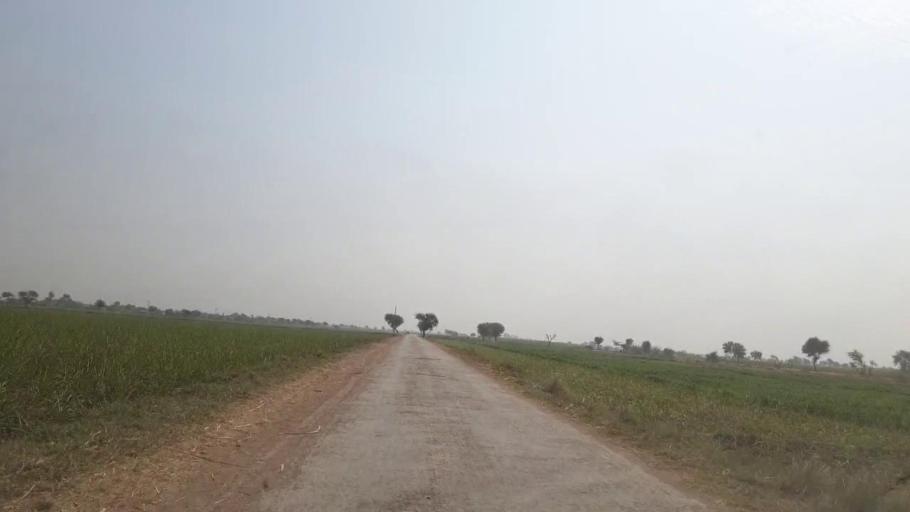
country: PK
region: Sindh
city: Mirpur Khas
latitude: 25.5418
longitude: 69.0855
